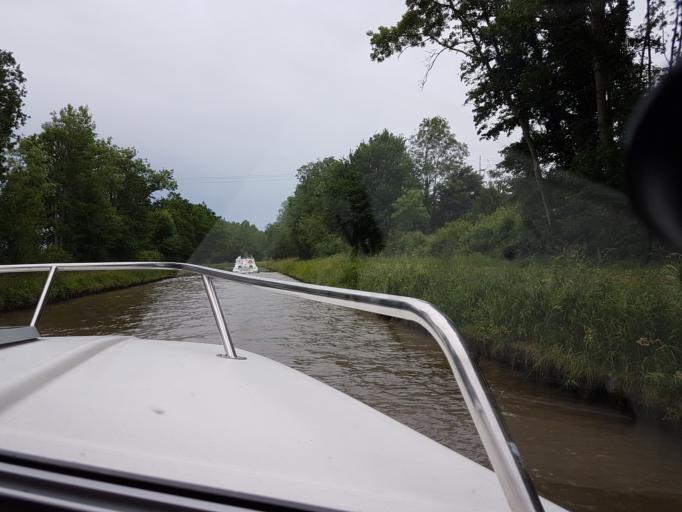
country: FR
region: Bourgogne
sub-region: Departement de la Nievre
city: Clamecy
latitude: 47.3922
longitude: 3.5997
